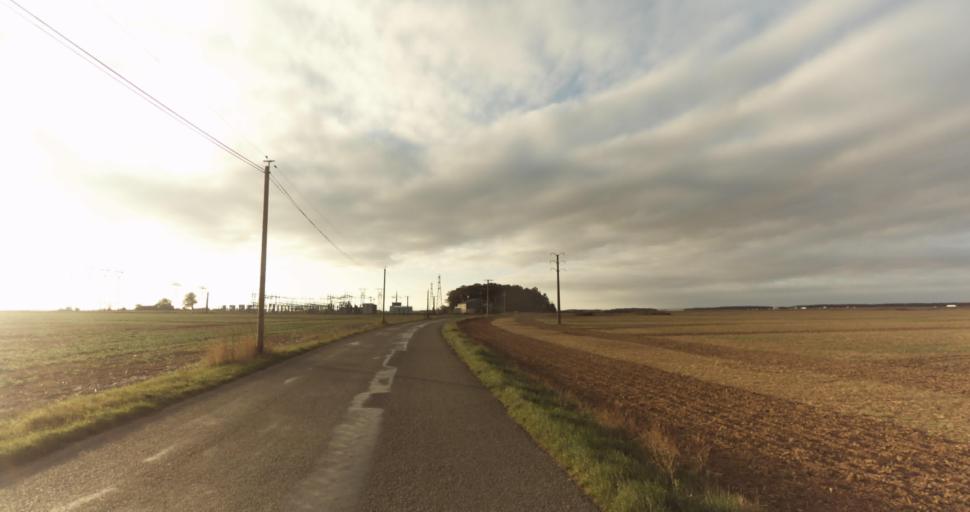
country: FR
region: Centre
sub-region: Departement d'Eure-et-Loir
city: Vernouillet
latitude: 48.7119
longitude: 1.3814
